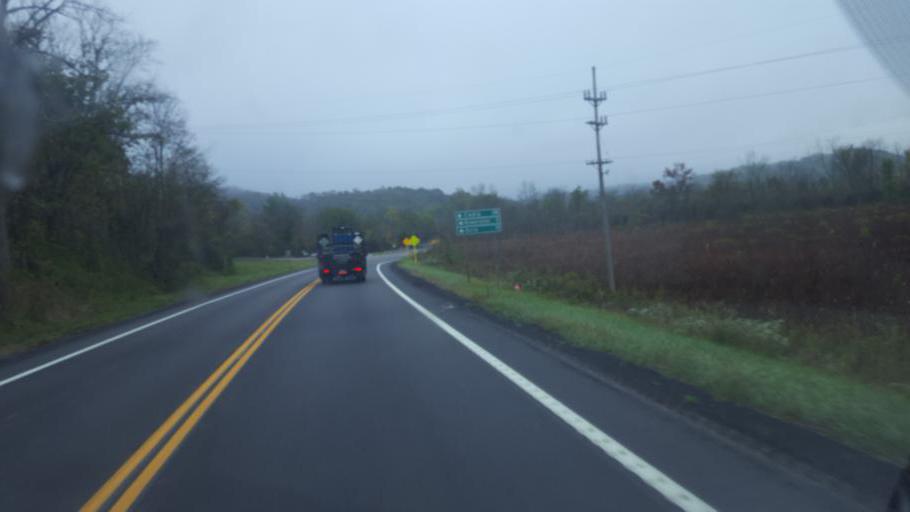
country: US
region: Ohio
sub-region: Tuscarawas County
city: Dennison
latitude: 40.3922
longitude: -81.2629
